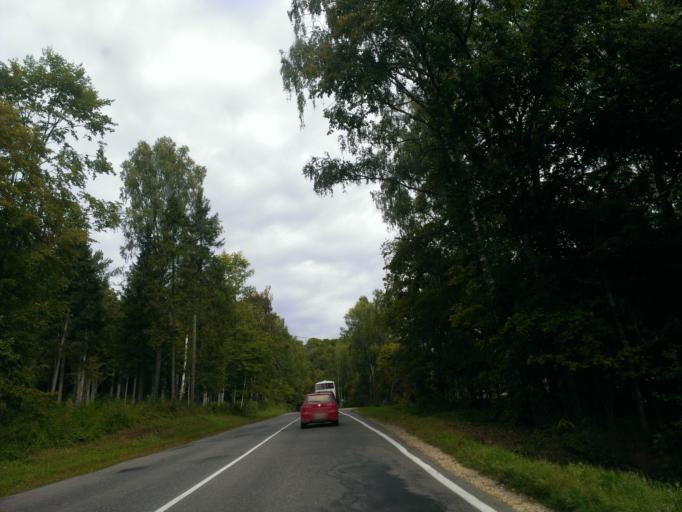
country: LV
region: Sigulda
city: Sigulda
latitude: 57.1780
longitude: 24.8478
